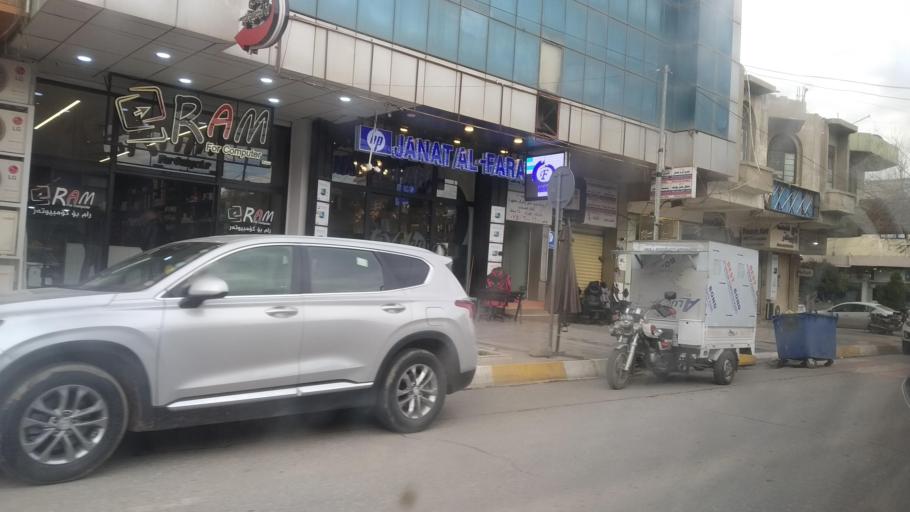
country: IQ
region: Arbil
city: Erbil
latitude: 36.1903
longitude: 44.0039
